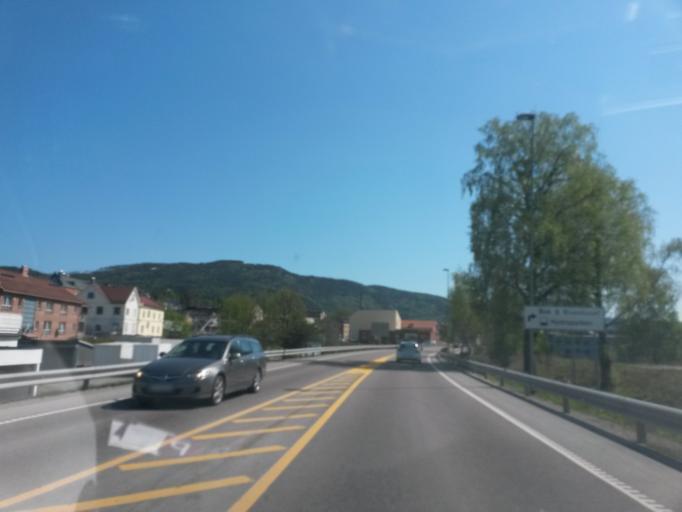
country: NO
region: Telemark
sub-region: Notodden
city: Notodden
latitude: 59.5593
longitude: 9.2505
